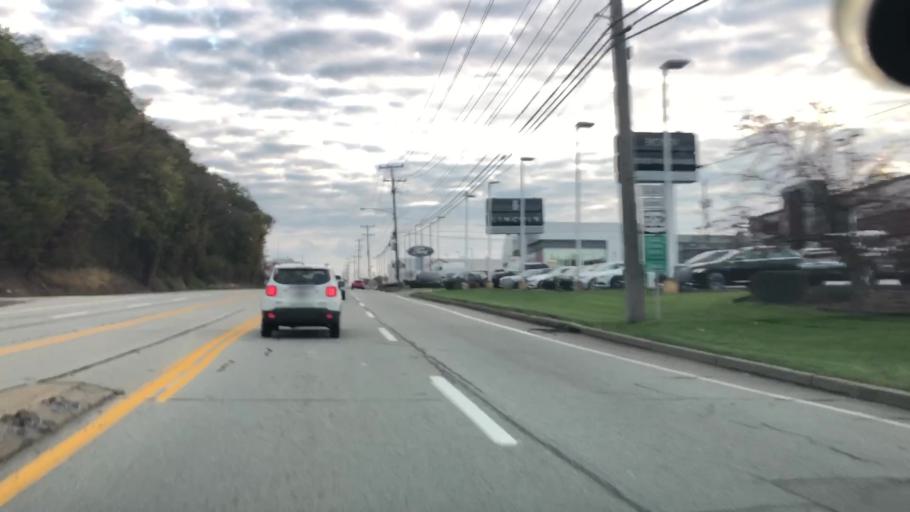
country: US
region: Pennsylvania
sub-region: Allegheny County
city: Monroeville
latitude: 40.4343
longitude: -79.7937
